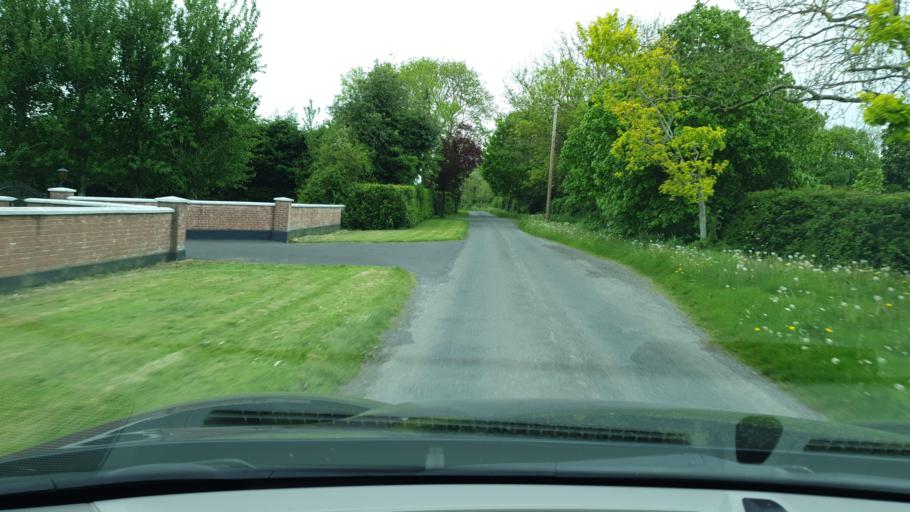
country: IE
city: Confey
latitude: 53.4105
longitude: -6.5257
